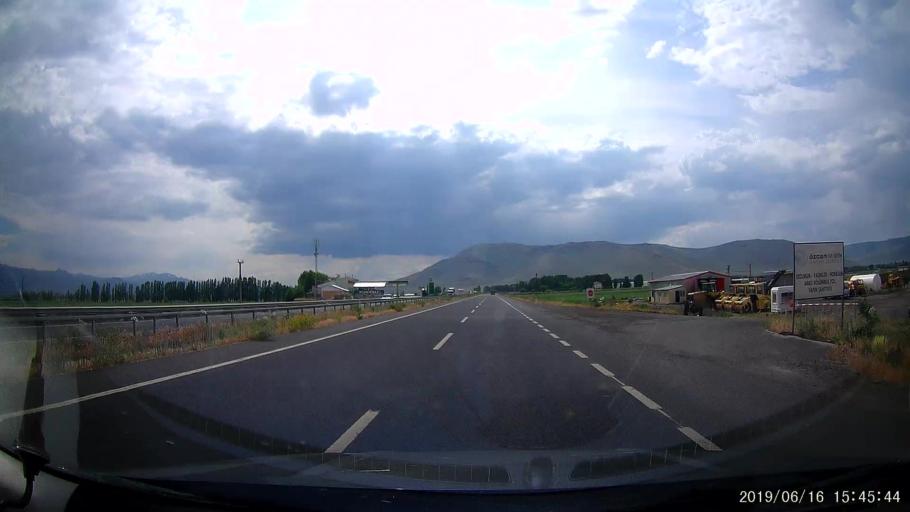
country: TR
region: Erzurum
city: Pasinler
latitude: 39.9891
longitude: 41.7595
